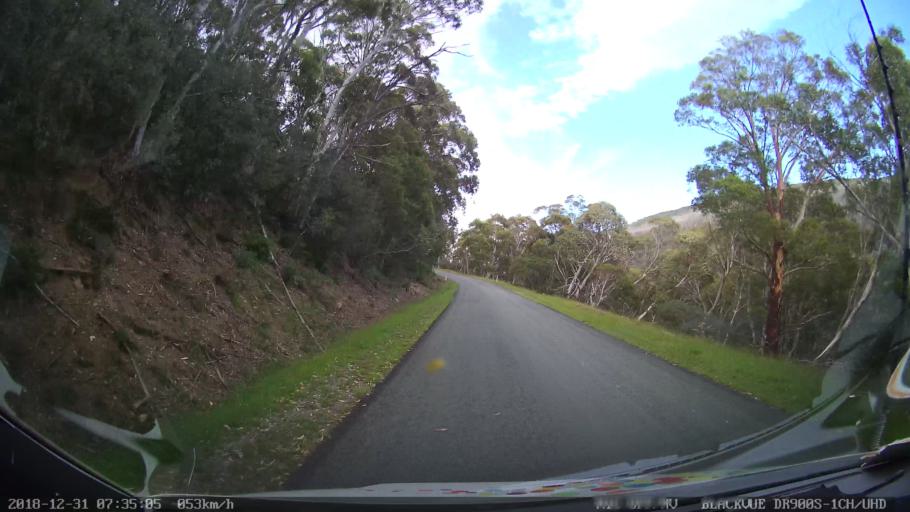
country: AU
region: New South Wales
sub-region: Snowy River
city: Jindabyne
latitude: -36.3328
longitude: 148.4467
